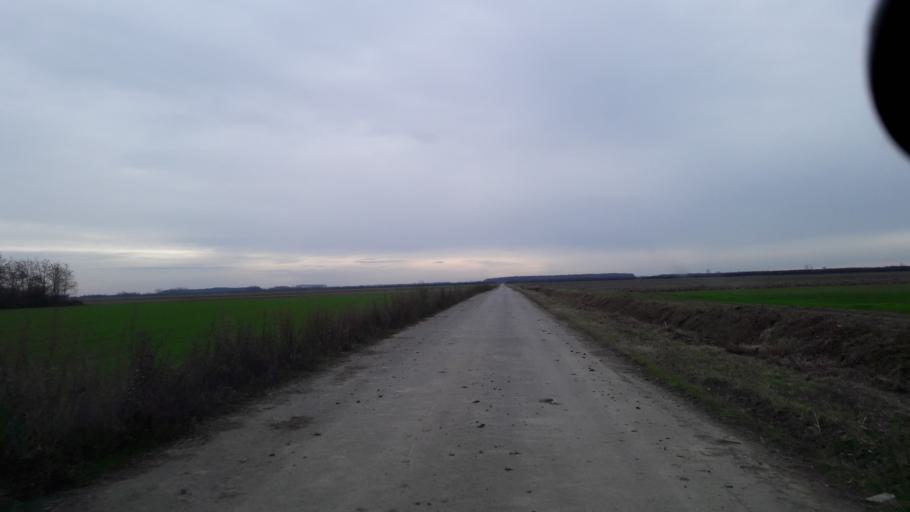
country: HR
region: Osjecko-Baranjska
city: Vladislavci
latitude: 45.4418
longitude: 18.5657
